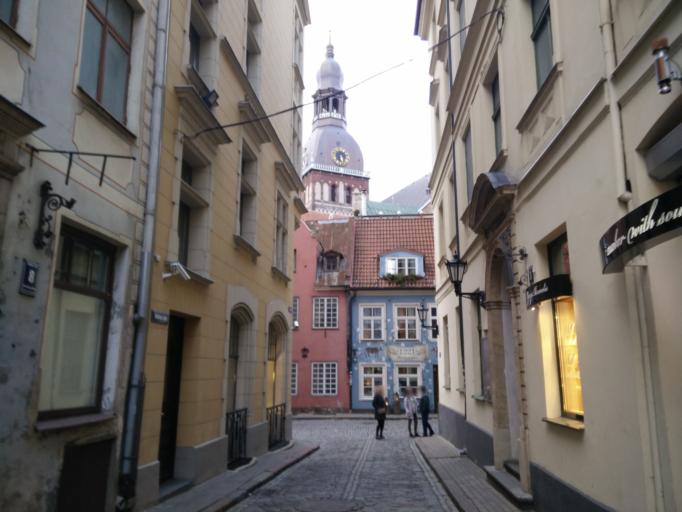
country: LV
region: Riga
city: Riga
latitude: 56.9485
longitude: 24.1059
